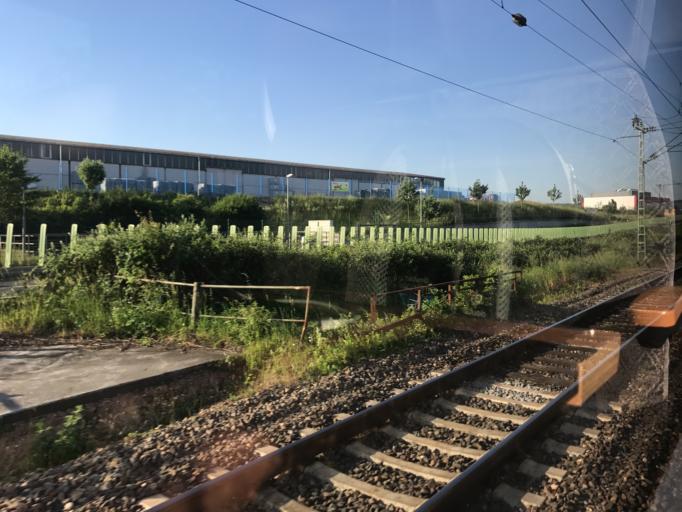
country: DE
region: Rheinland-Pfalz
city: Nieder-Ingelheim
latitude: 49.9842
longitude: 8.0649
